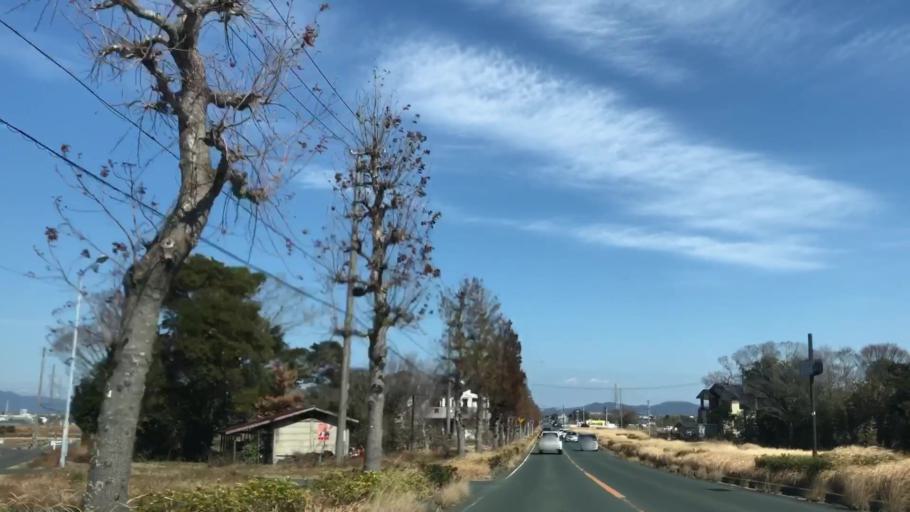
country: JP
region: Aichi
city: Toyohashi
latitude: 34.7148
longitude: 137.3631
